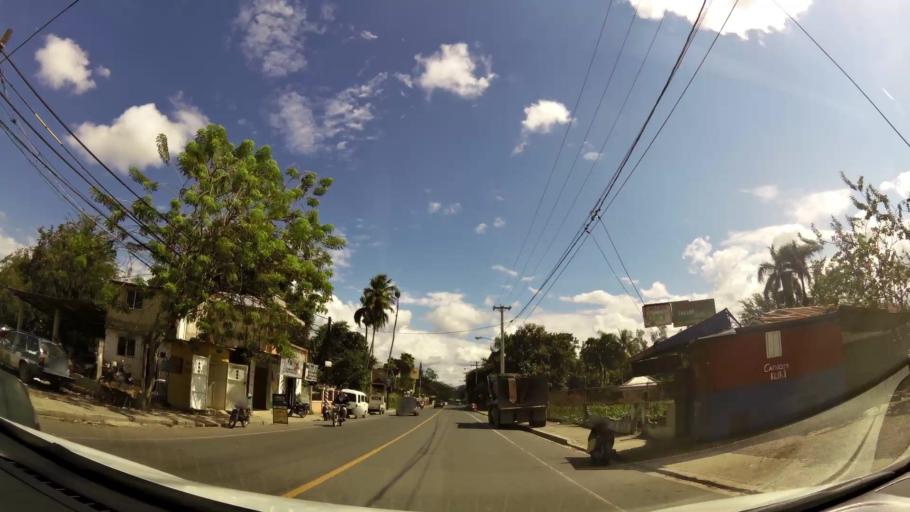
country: DO
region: La Vega
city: Concepcion de La Vega
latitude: 19.2391
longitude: -70.5352
